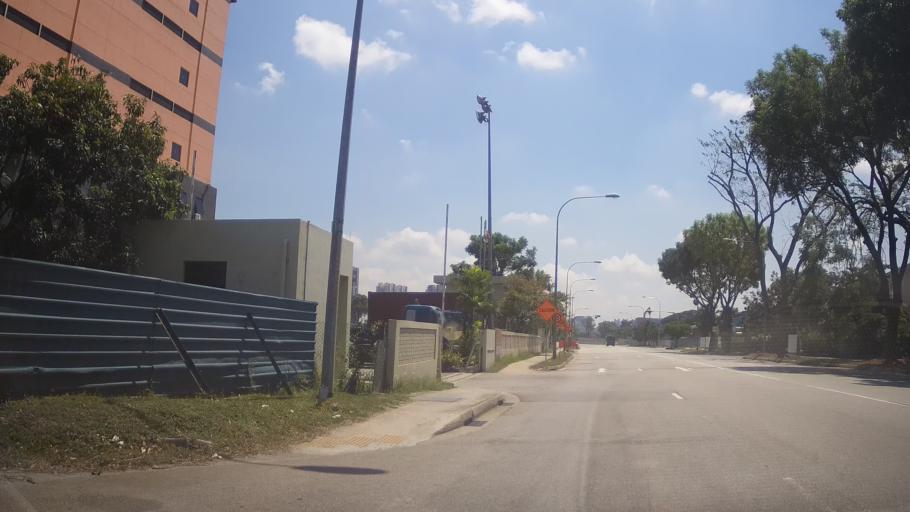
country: SG
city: Singapore
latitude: 1.3203
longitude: 103.7216
